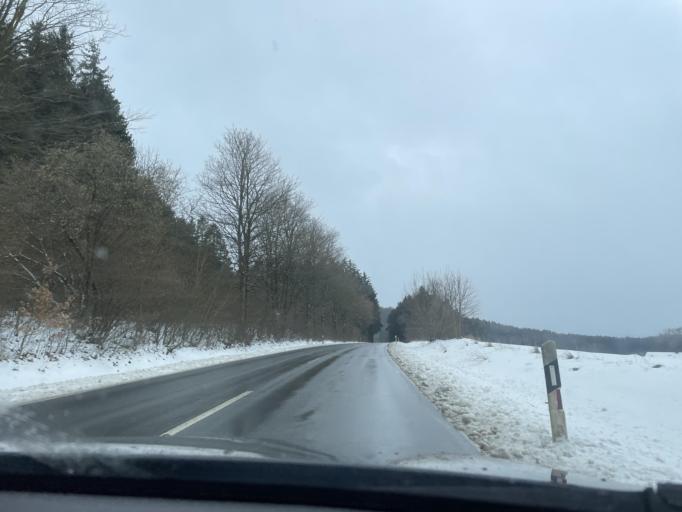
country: DE
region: Bavaria
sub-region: Upper Palatinate
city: Rimbach
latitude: 49.2285
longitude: 12.8579
